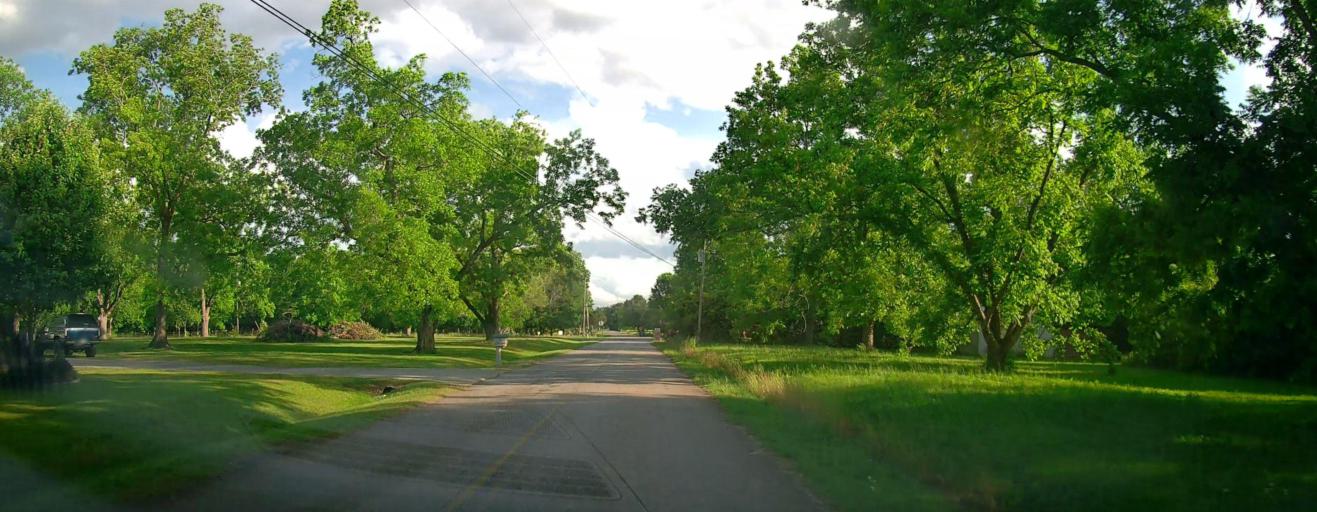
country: US
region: Georgia
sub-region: Peach County
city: Byron
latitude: 32.6437
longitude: -83.7919
